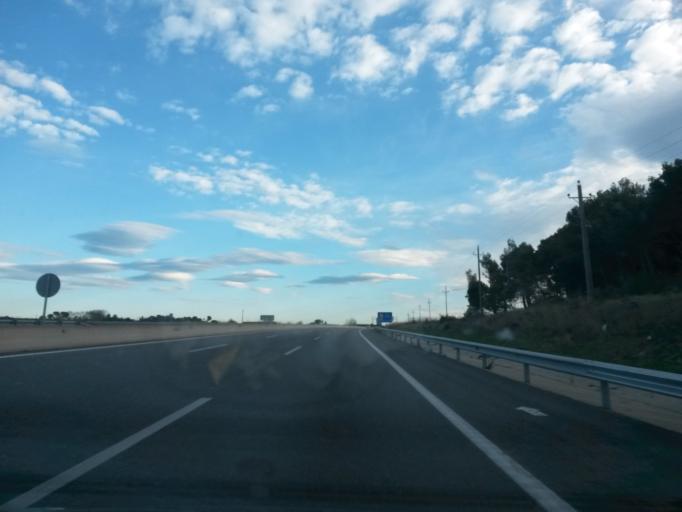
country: ES
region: Catalonia
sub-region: Provincia de Girona
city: Vilademuls
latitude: 42.1223
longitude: 2.9120
